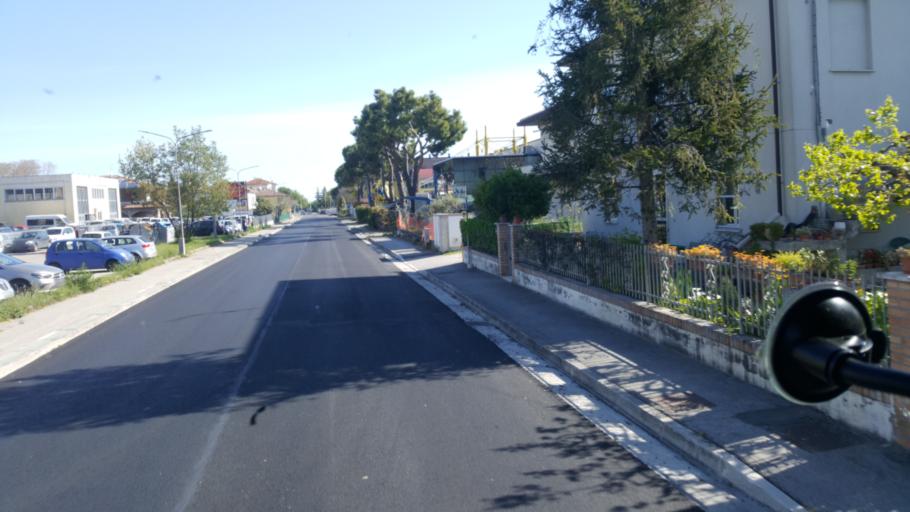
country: IT
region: Emilia-Romagna
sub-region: Provincia di Rimini
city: Poggio Berni
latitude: 44.0122
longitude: 12.4065
